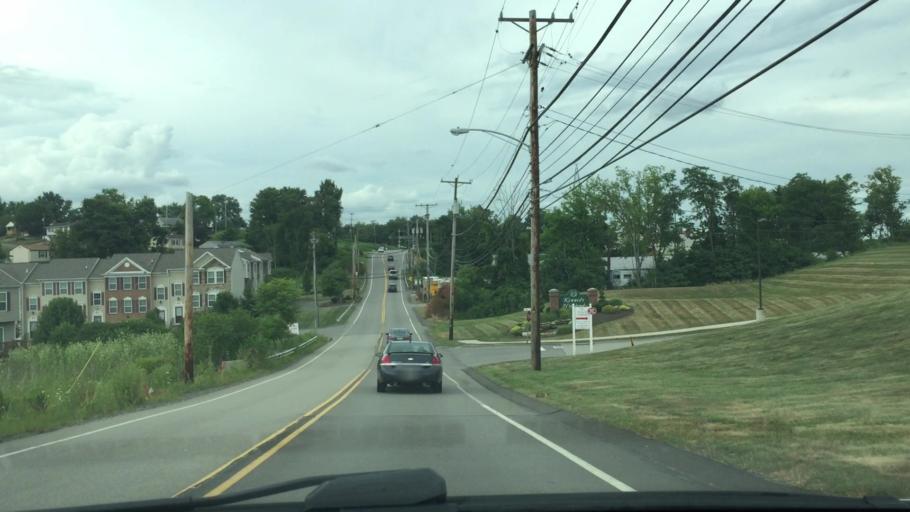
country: US
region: Pennsylvania
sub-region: Allegheny County
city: McKees Rocks
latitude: 40.4655
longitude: -80.0999
